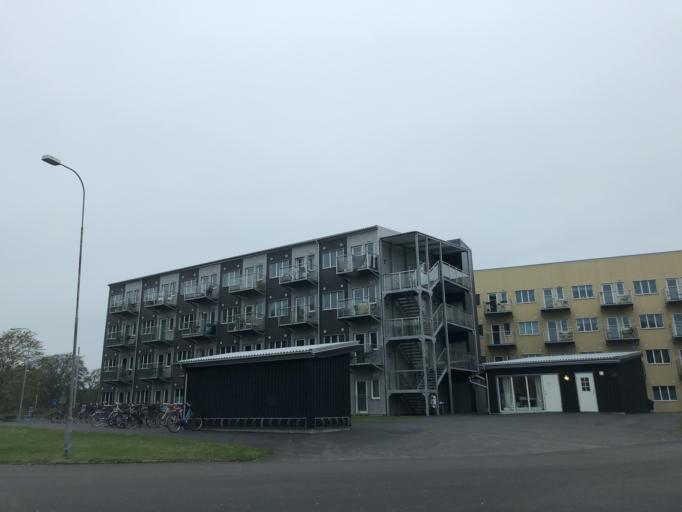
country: SE
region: Vaestra Goetaland
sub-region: Goteborg
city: Majorna
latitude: 57.6572
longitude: 11.8846
